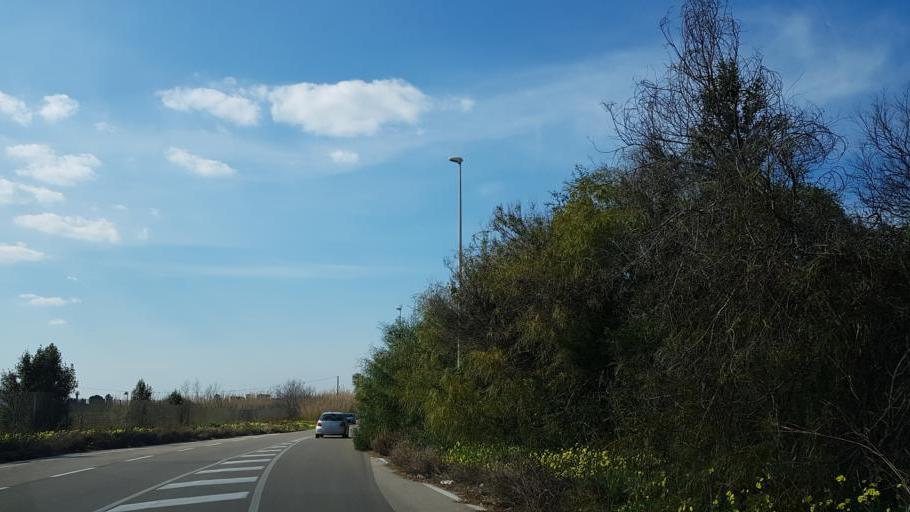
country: IT
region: Apulia
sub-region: Provincia di Brindisi
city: Brindisi
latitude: 40.6808
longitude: 17.8960
